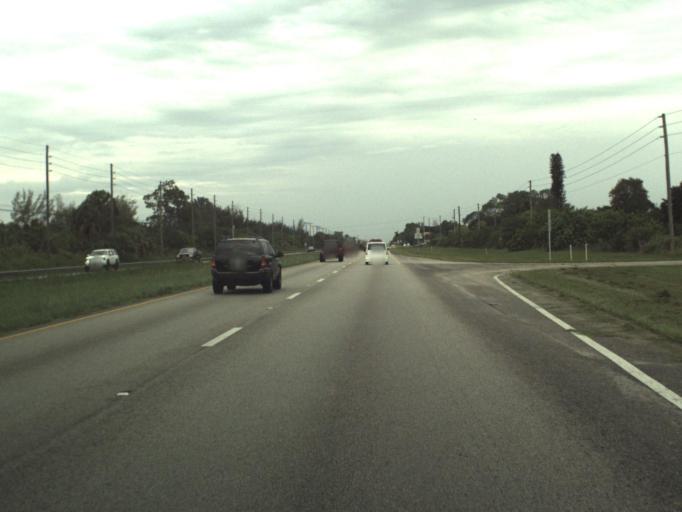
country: US
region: Florida
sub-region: Palm Beach County
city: Loxahatchee Groves
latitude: 26.6825
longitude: -80.2695
